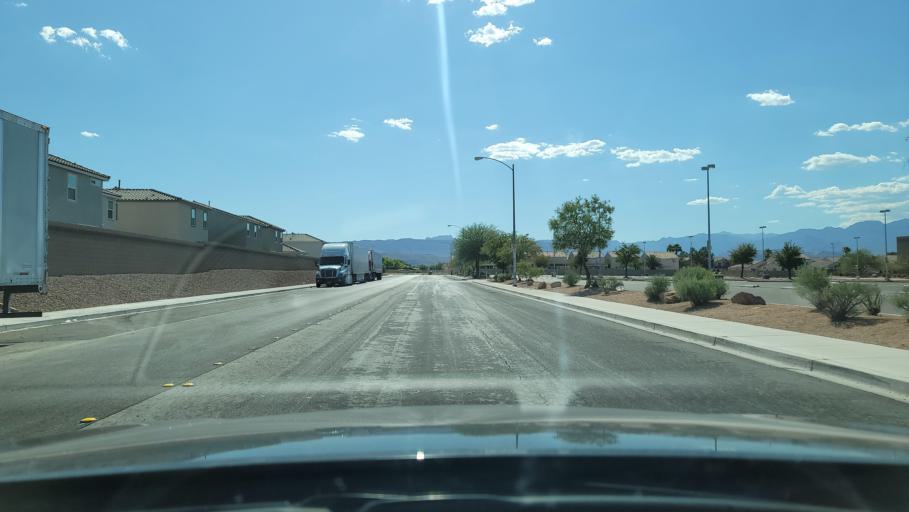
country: US
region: Nevada
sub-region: Clark County
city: Spring Valley
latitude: 36.0870
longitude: -115.2461
